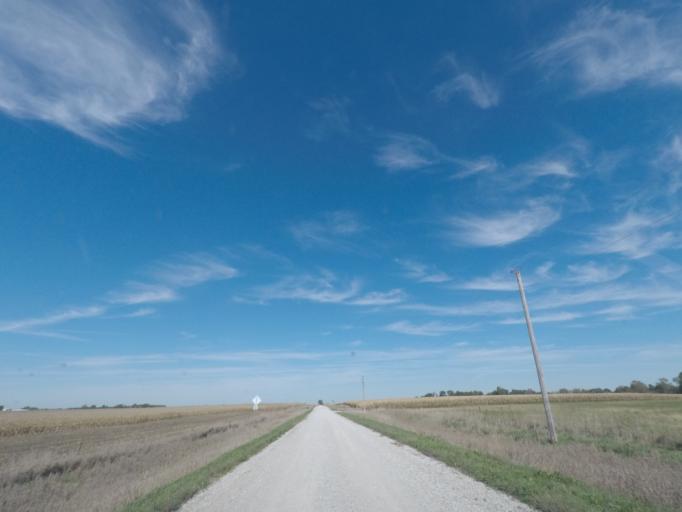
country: US
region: Iowa
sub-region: Story County
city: Nevada
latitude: 42.0139
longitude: -93.3573
